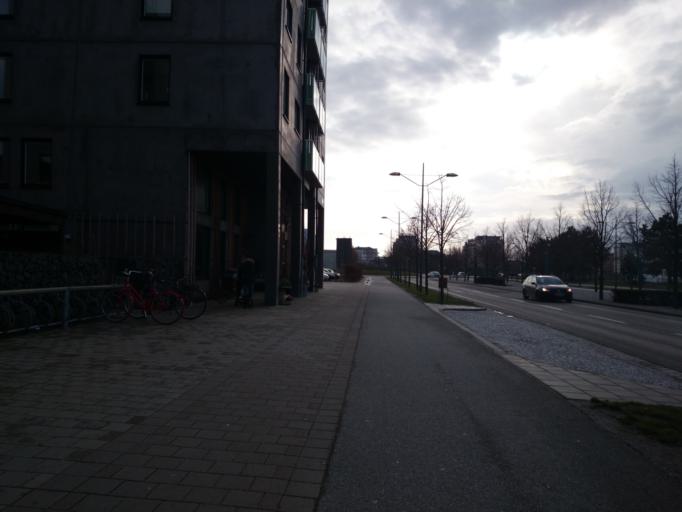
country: SE
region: Skane
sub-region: Malmo
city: Malmoe
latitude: 55.6077
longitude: 12.9789
